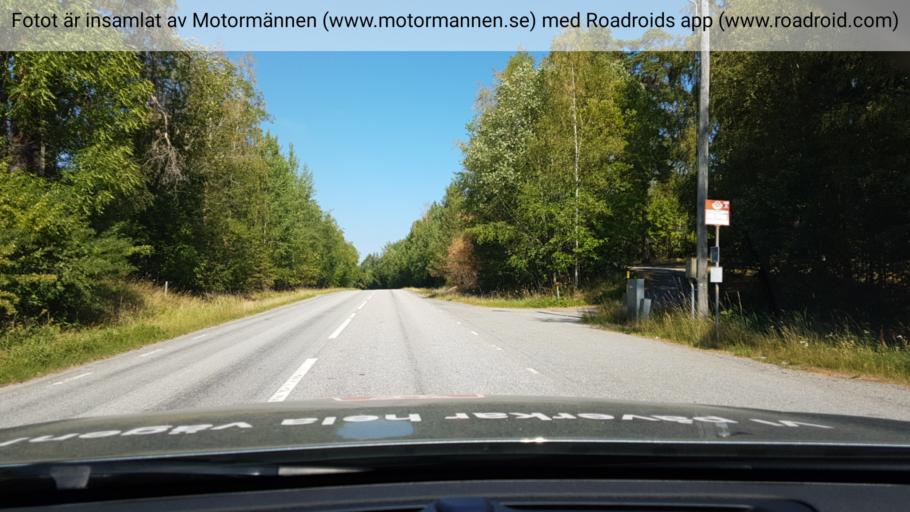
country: SE
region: Stockholm
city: Stenhamra
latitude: 59.3873
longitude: 17.5779
